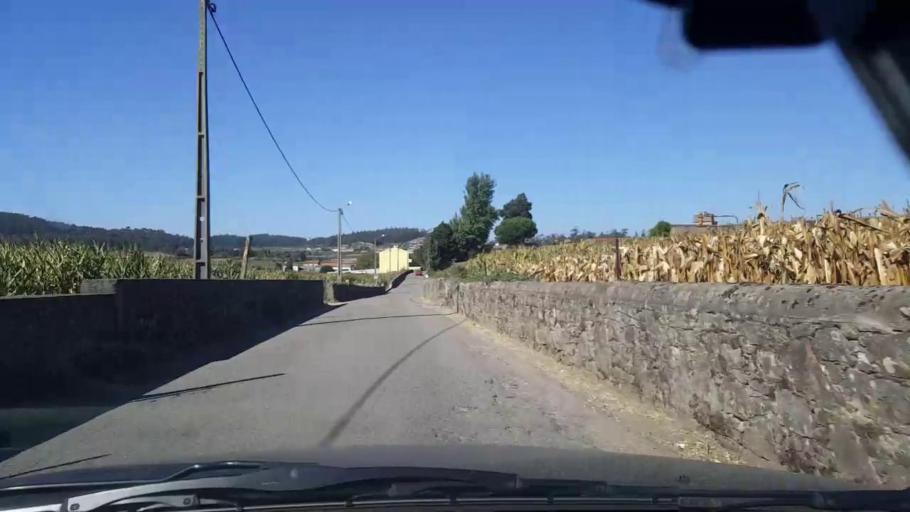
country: PT
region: Braga
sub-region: Vila Nova de Famalicao
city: Ribeirao
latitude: 41.3699
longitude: -8.6449
